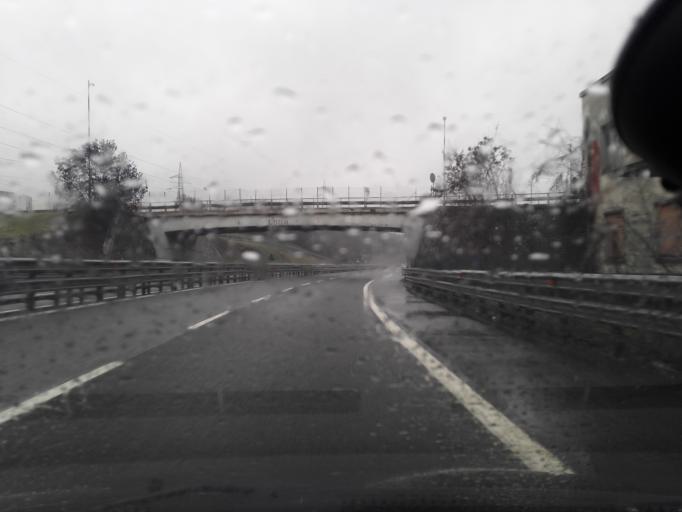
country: IT
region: Piedmont
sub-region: Provincia di Alessandria
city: Vignole Borbera
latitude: 44.7027
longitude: 8.8874
